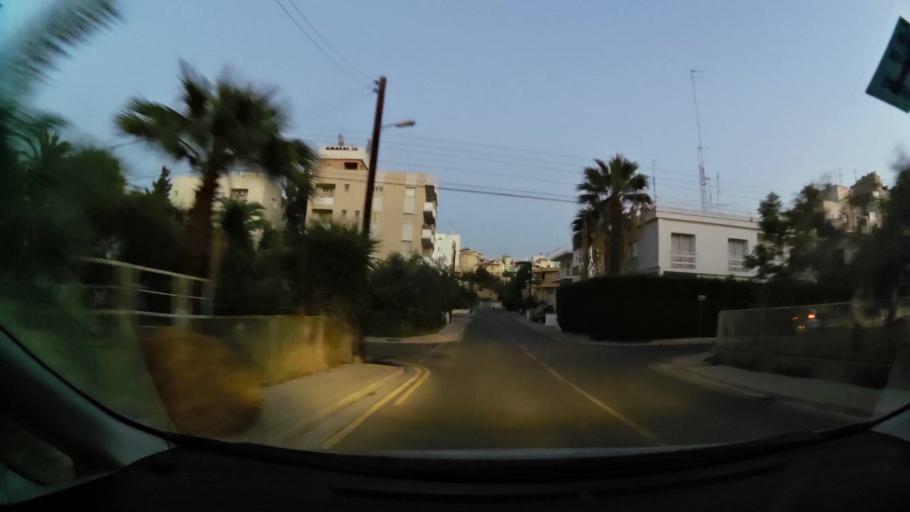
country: CY
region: Lefkosia
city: Nicosia
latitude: 35.1633
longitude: 33.3686
